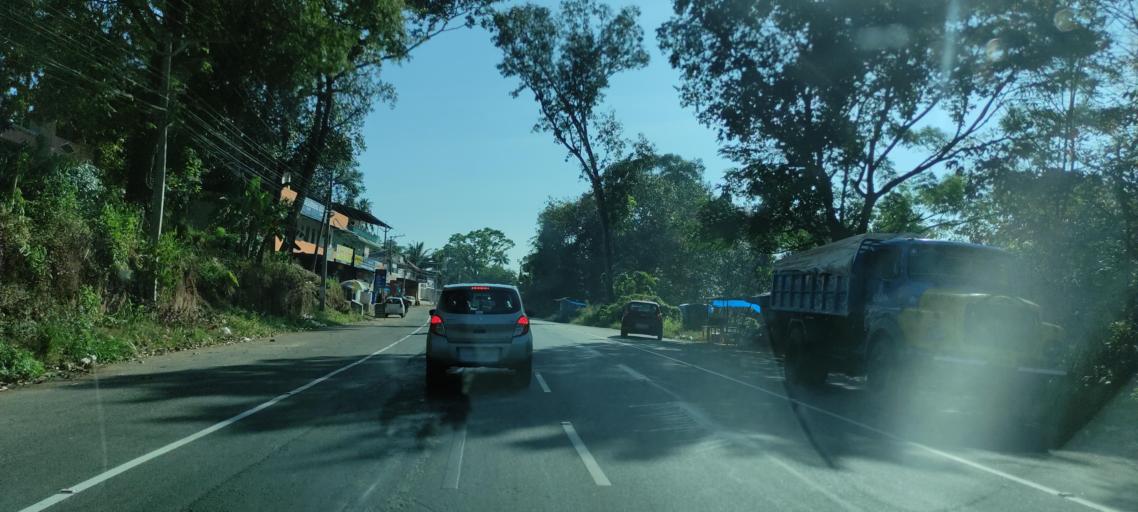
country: IN
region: Kerala
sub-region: Pattanamtitta
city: Adur
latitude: 9.1633
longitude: 76.7024
